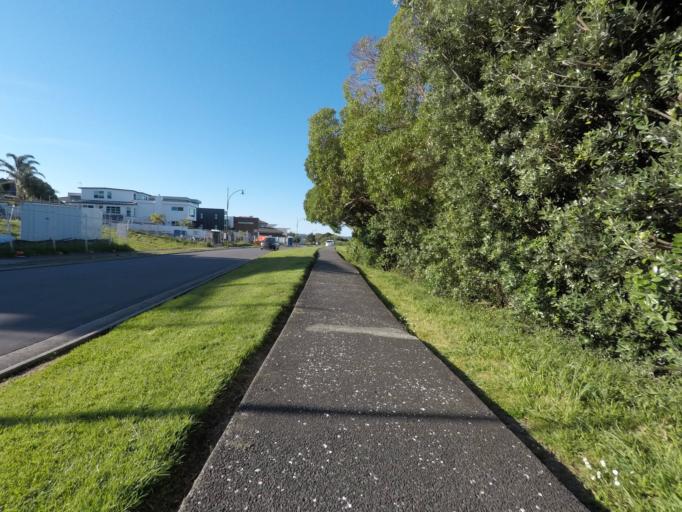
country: NZ
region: Auckland
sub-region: Auckland
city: Rosebank
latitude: -36.8358
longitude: 174.6618
